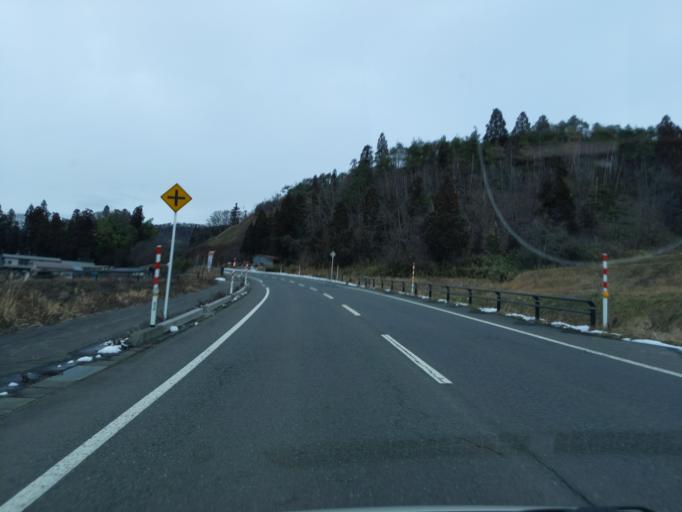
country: JP
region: Iwate
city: Mizusawa
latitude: 39.1734
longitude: 141.2643
